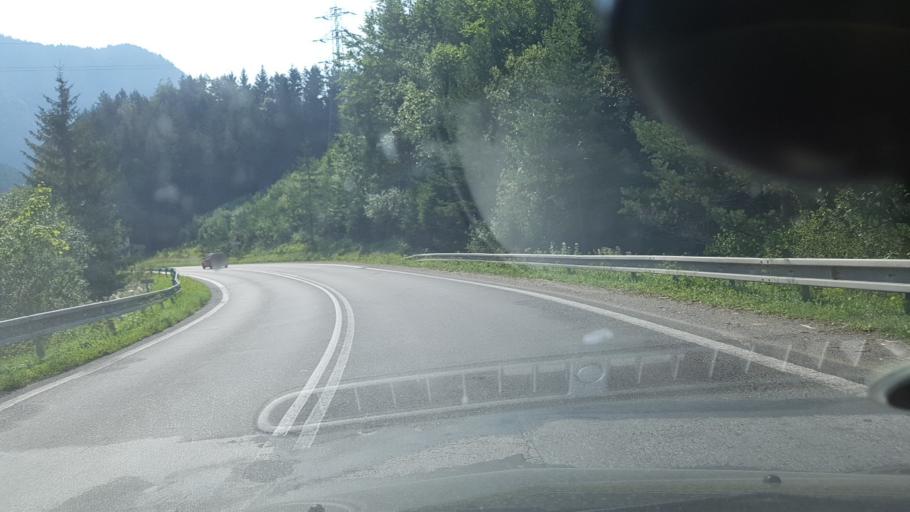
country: SK
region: Zilinsky
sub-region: Okres Dolny Kubin
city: Dolny Kubin
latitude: 49.1471
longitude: 19.2844
